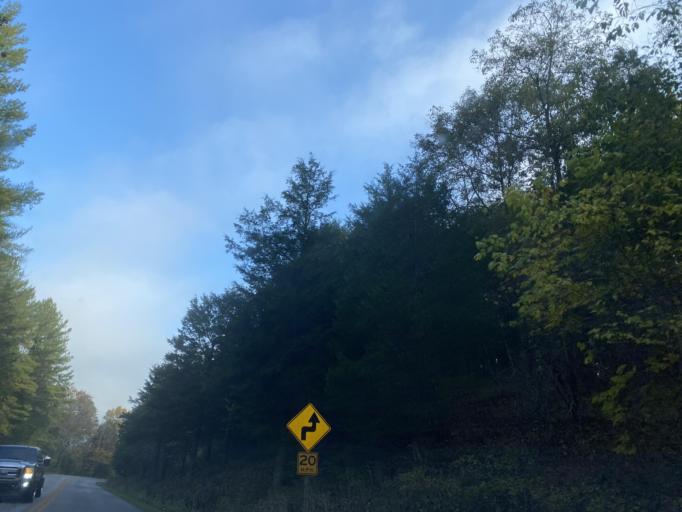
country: US
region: Kentucky
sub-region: Pendleton County
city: Falmouth
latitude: 38.7205
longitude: -84.2862
